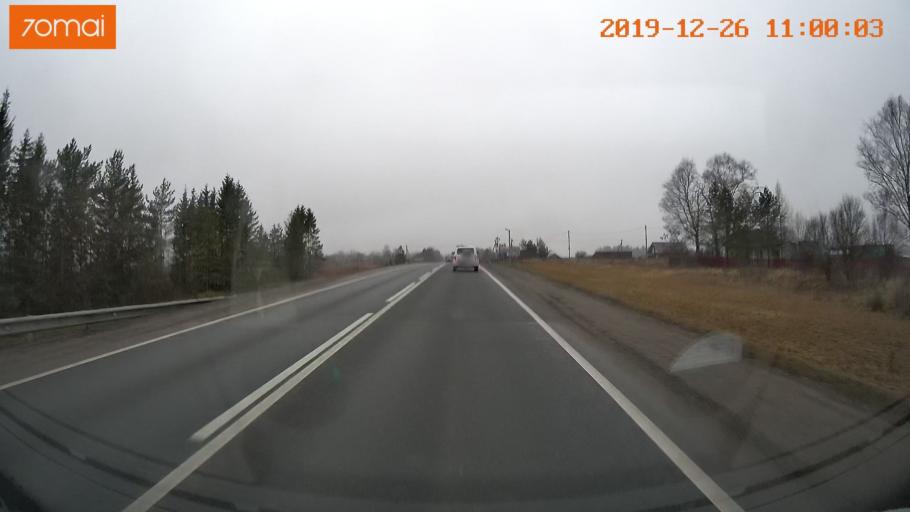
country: RU
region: Vologda
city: Molochnoye
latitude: 59.1679
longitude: 39.4569
